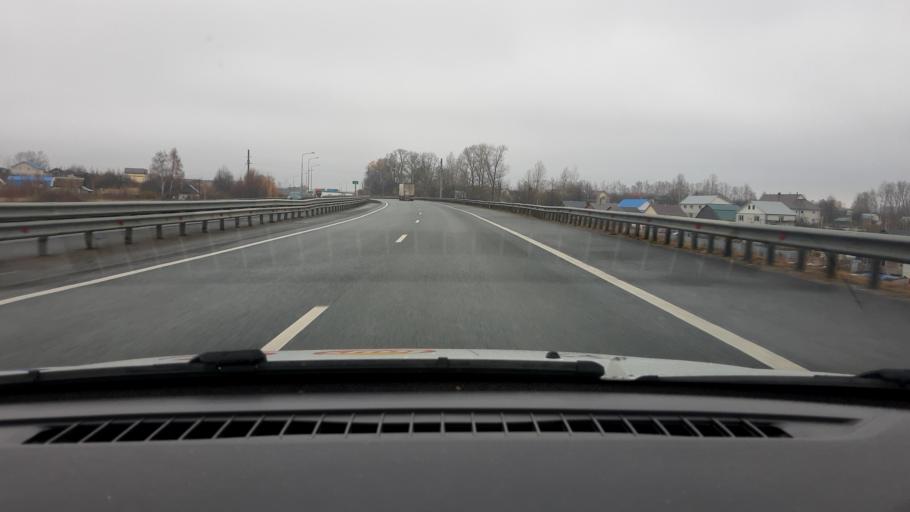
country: RU
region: Nizjnij Novgorod
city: Burevestnik
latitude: 56.1639
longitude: 43.7497
